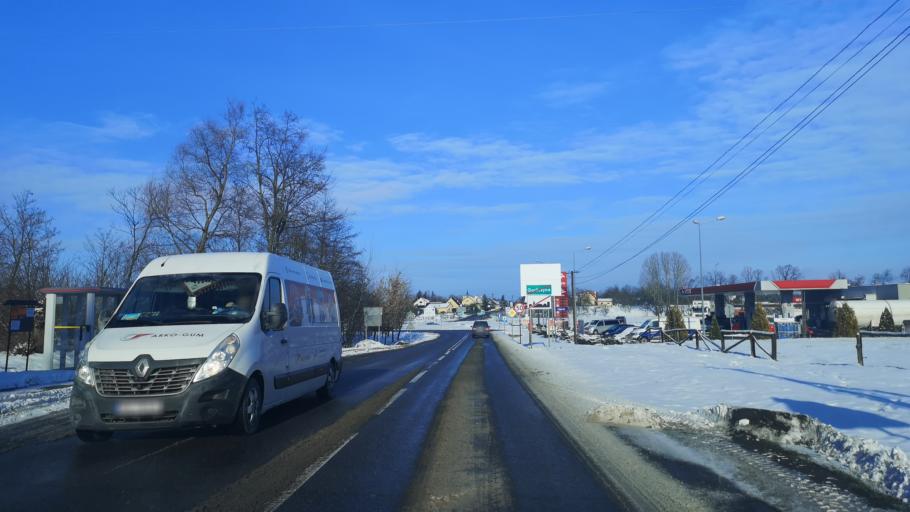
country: PL
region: Subcarpathian Voivodeship
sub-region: Powiat przeworski
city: Gorliczyna
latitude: 50.0953
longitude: 22.4922
